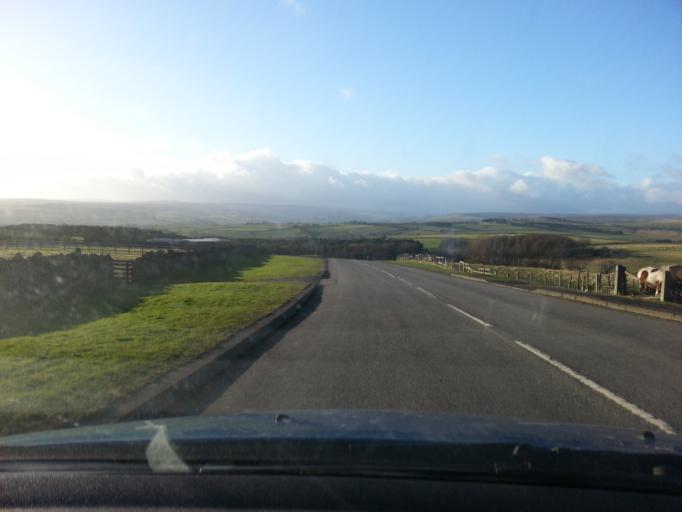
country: GB
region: England
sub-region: County Durham
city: Tow Law
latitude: 54.7429
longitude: -1.8185
